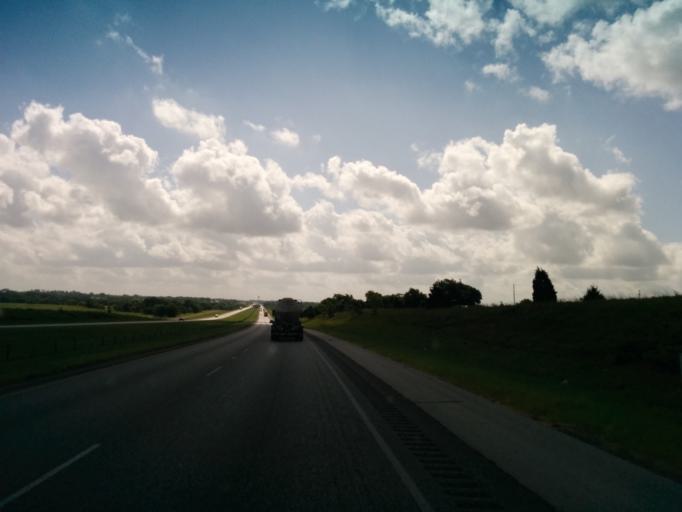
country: US
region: Texas
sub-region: Fayette County
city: Schulenburg
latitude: 29.6886
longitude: -96.9559
